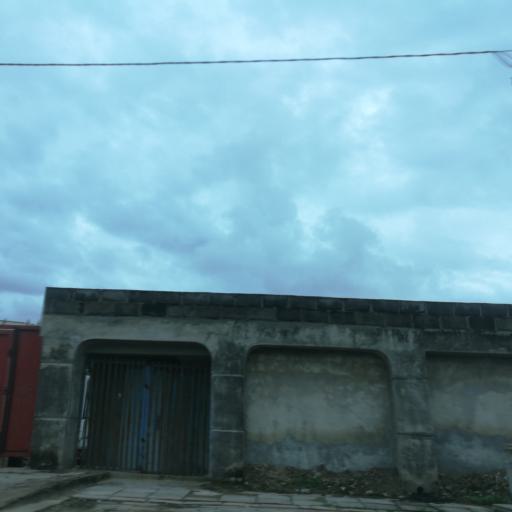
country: NG
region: Lagos
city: Ikoyi
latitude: 6.4477
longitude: 3.4671
